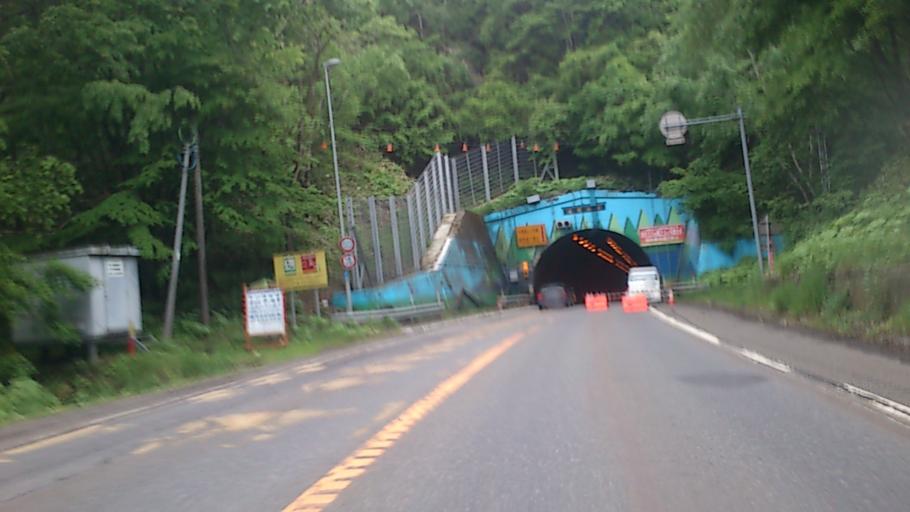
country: JP
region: Hokkaido
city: Obihiro
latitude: 42.8211
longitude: 143.7111
